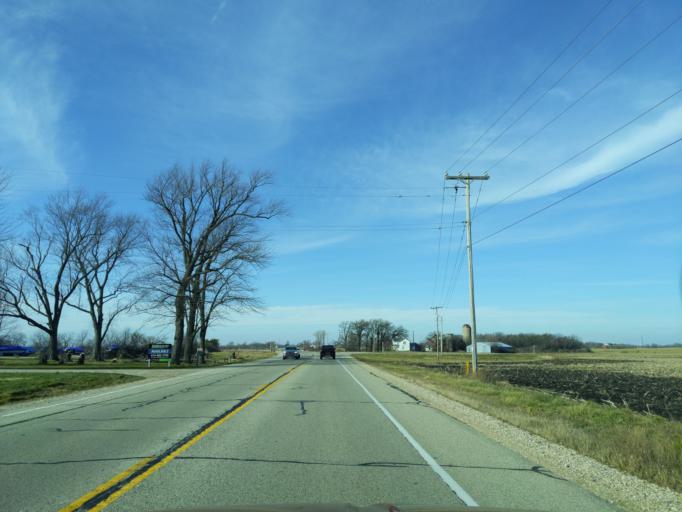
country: US
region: Wisconsin
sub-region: Walworth County
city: Whitewater
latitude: 42.8147
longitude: -88.6886
